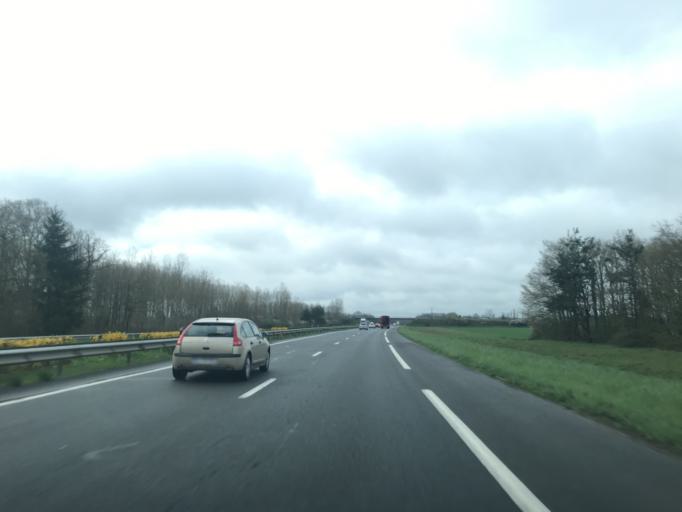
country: FR
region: Centre
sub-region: Departement du Loiret
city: Chateauneuf-sur-Loire
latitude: 47.8855
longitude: 2.2229
